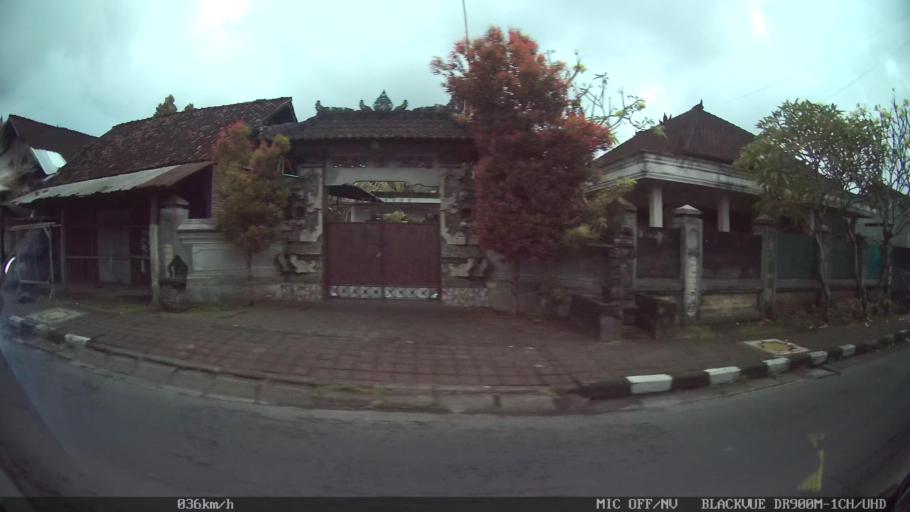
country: ID
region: Bali
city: Banjar Cemenggon
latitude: -8.5402
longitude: 115.2022
